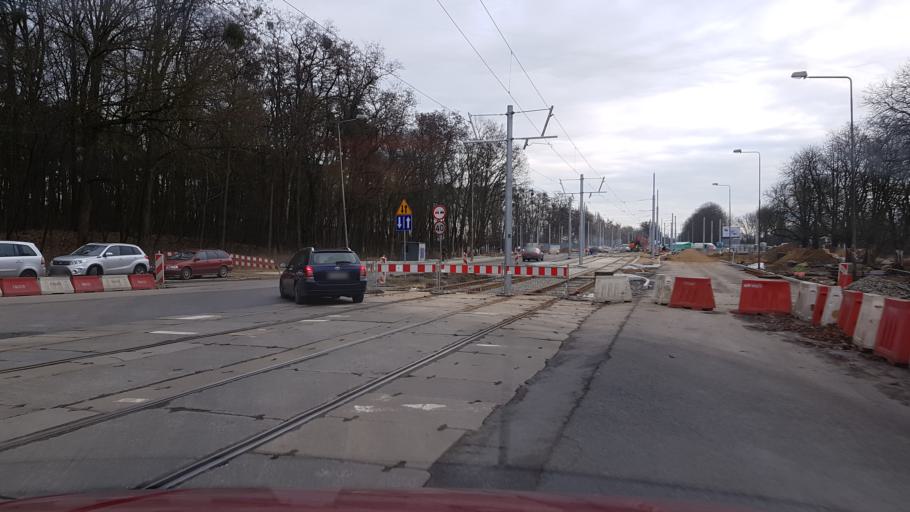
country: PL
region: West Pomeranian Voivodeship
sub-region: Szczecin
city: Szczecin
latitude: 53.4597
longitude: 14.5001
